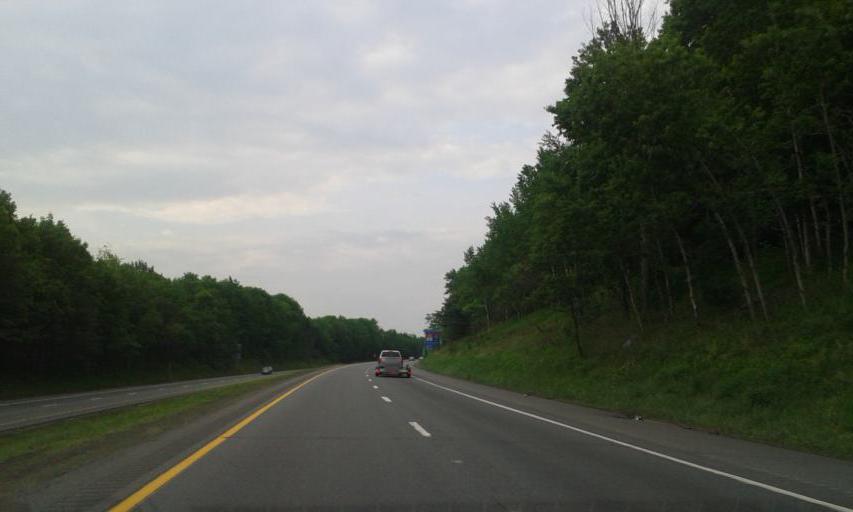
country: US
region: Pennsylvania
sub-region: Susquehanna County
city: Susquehanna
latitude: 41.8052
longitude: -75.6879
